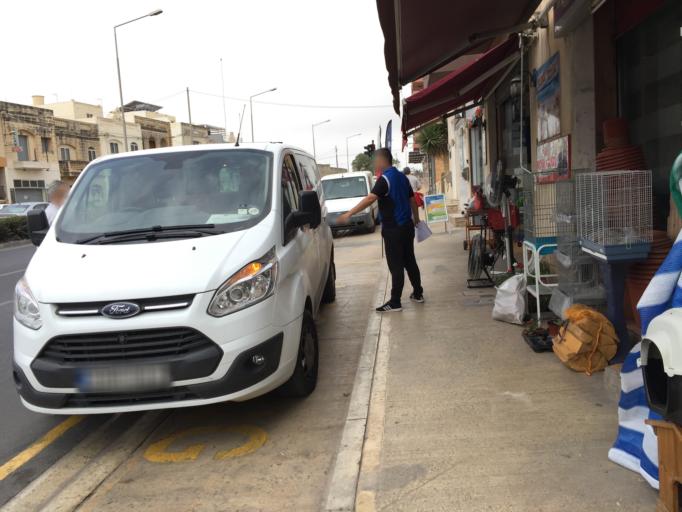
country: MT
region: Haz-Zabbar
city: Zabbar
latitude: 35.8712
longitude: 14.5355
